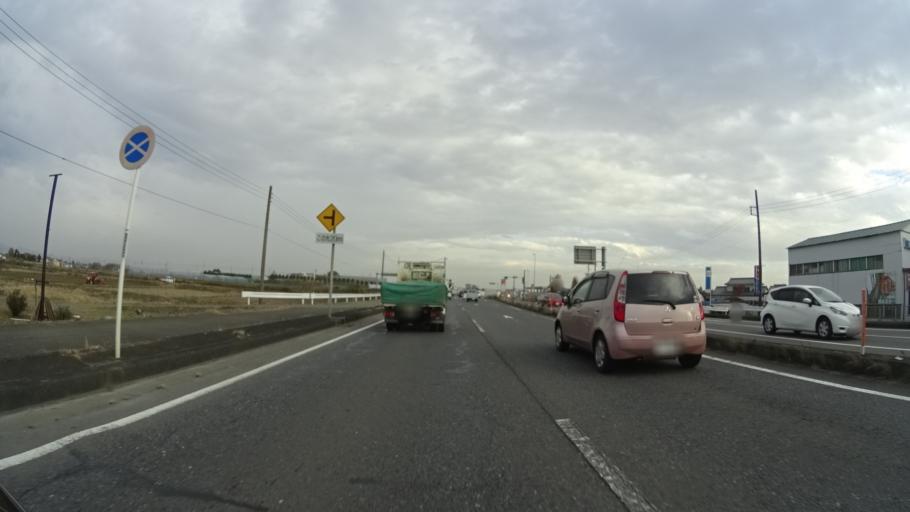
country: JP
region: Gunma
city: Isesaki
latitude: 36.3602
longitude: 139.1961
